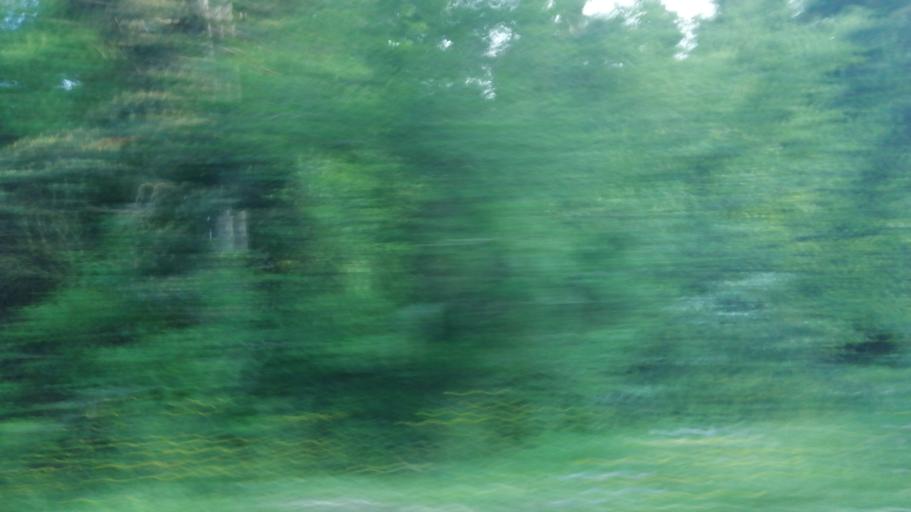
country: TR
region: Karabuk
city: Eskipazar
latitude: 41.0459
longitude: 32.5480
